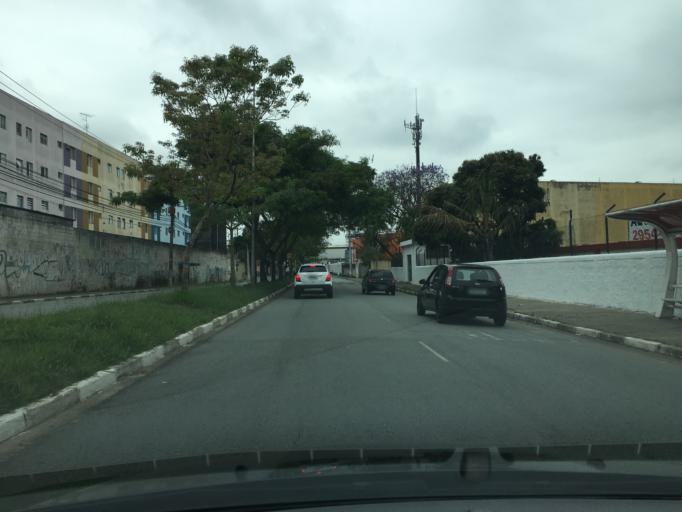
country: BR
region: Sao Paulo
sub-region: Guarulhos
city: Guarulhos
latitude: -23.4818
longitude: -46.5377
